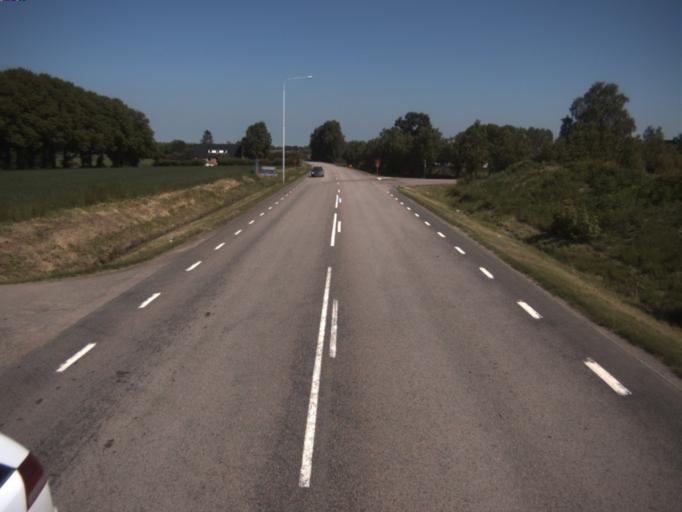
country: SE
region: Skane
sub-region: Helsingborg
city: Barslov
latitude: 56.0186
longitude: 12.7944
